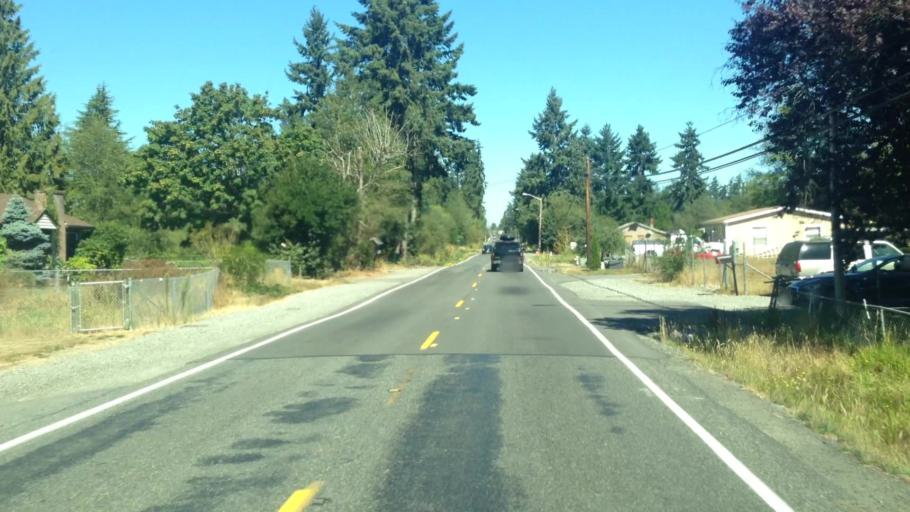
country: US
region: Washington
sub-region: Pierce County
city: Parkland
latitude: 47.1505
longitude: -122.4155
